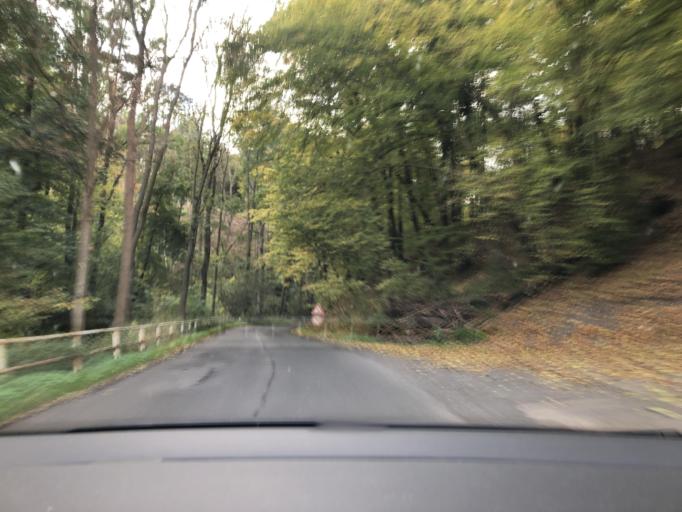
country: CZ
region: Ustecky
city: Velke Brezno
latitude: 50.6330
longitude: 14.1596
